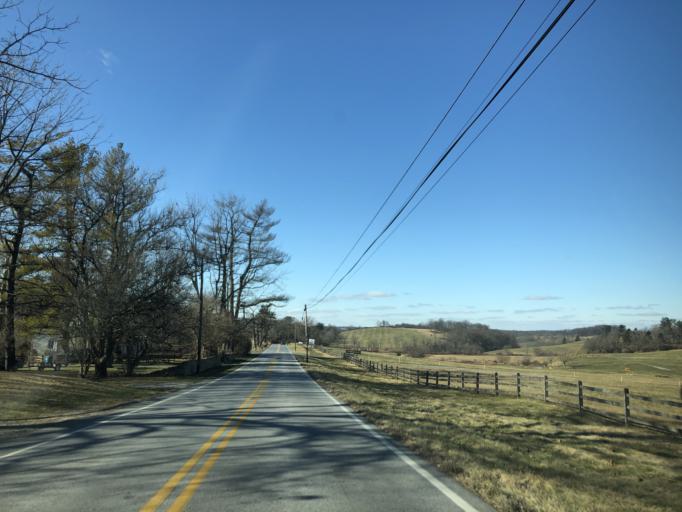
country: US
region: Pennsylvania
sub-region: Chester County
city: Upland
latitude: 39.9005
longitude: -75.7686
